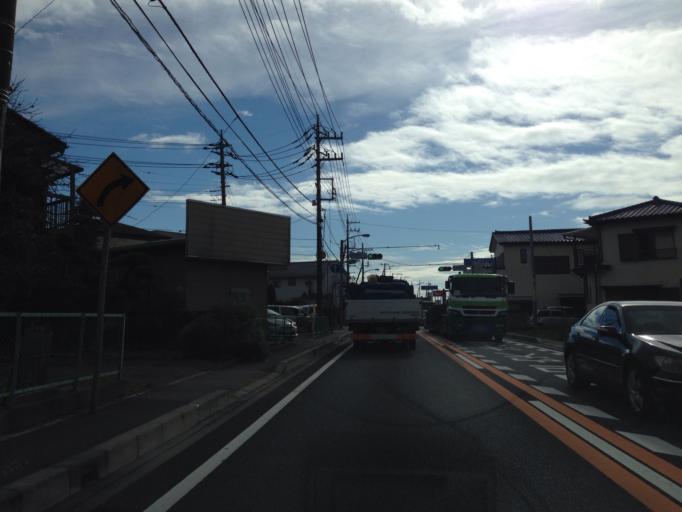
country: JP
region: Ibaraki
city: Ushiku
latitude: 35.9721
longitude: 140.1395
